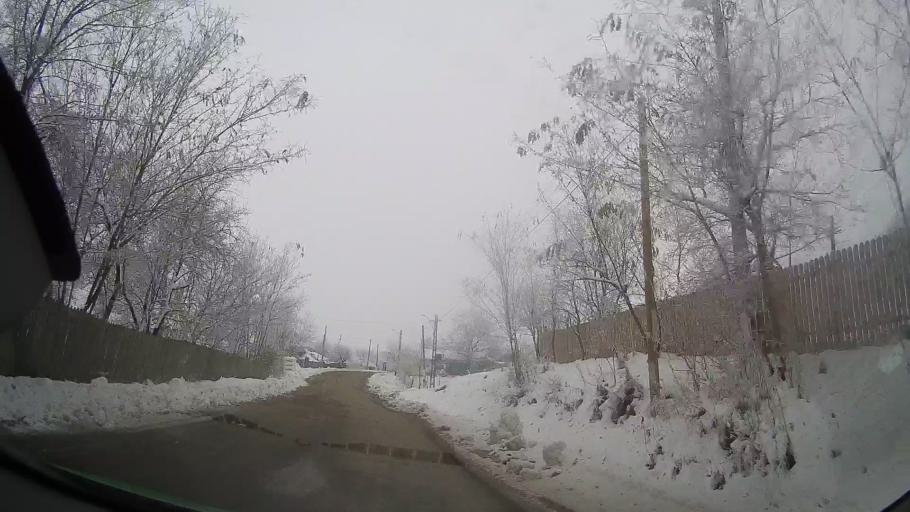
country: RO
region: Iasi
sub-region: Comuna Tansa
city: Tansa
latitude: 46.9124
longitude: 27.2261
